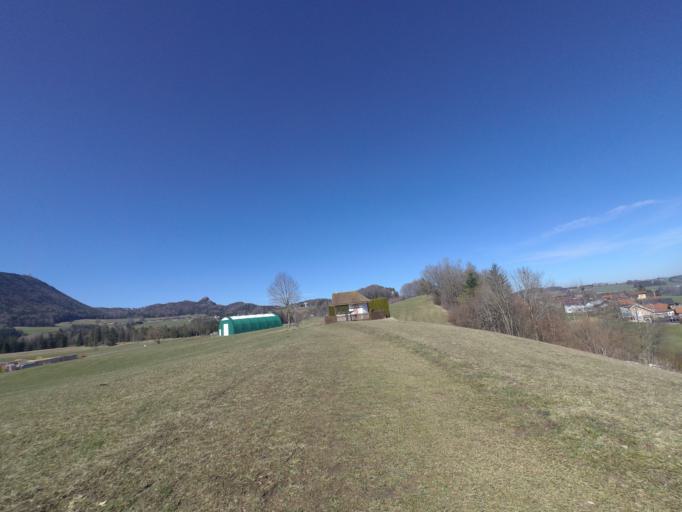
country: AT
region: Salzburg
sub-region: Politischer Bezirk Salzburg-Umgebung
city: Koppl
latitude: 47.8080
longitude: 13.1545
